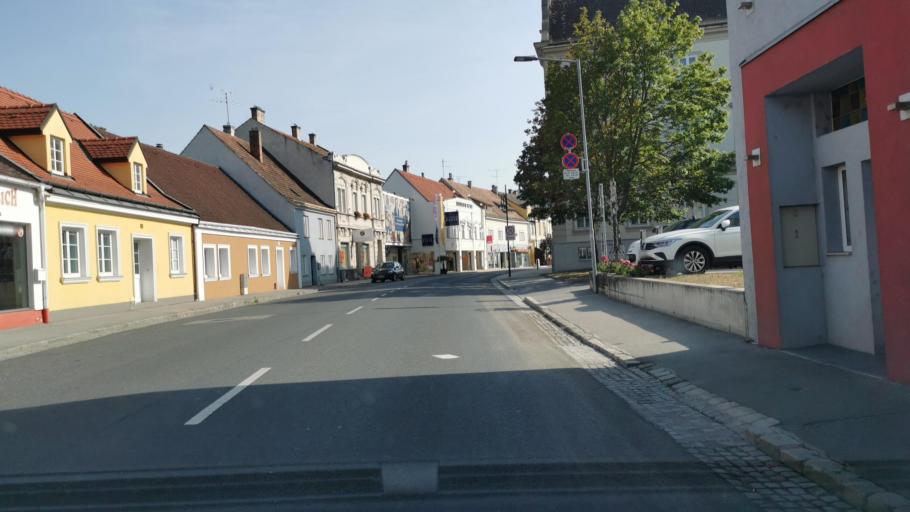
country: AT
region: Lower Austria
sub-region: Politischer Bezirk Mistelbach
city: Mistelbach
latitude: 48.5713
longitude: 16.5725
